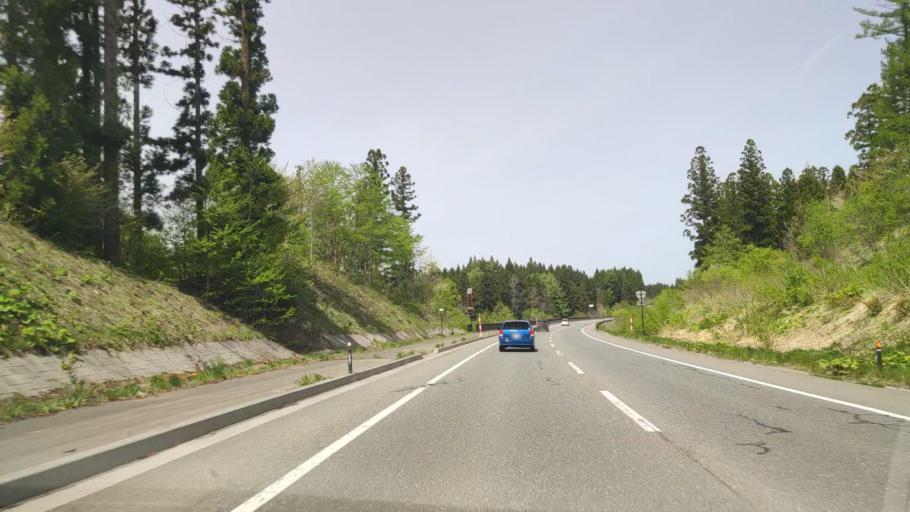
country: JP
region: Aomori
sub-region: Misawa Shi
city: Inuotose
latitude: 40.6891
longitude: 141.1689
